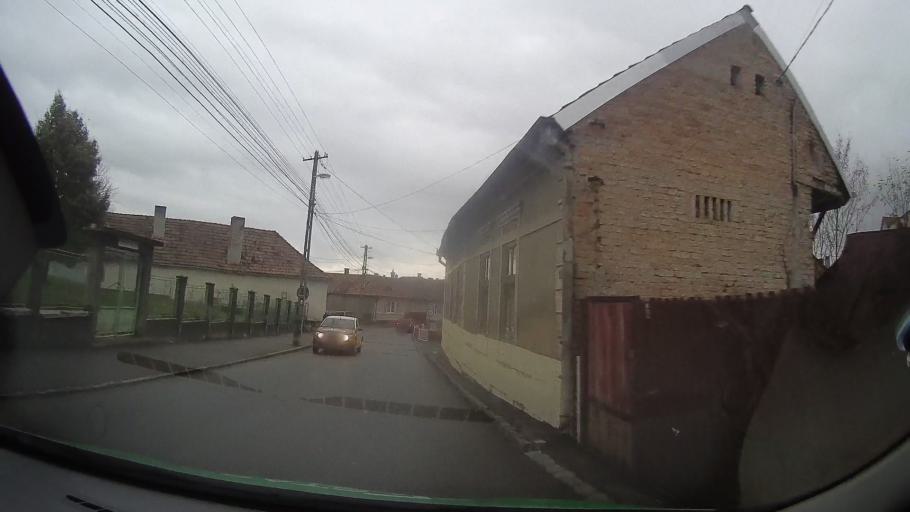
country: RO
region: Mures
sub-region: Municipiul Reghin
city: Reghin
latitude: 46.7806
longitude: 24.7060
